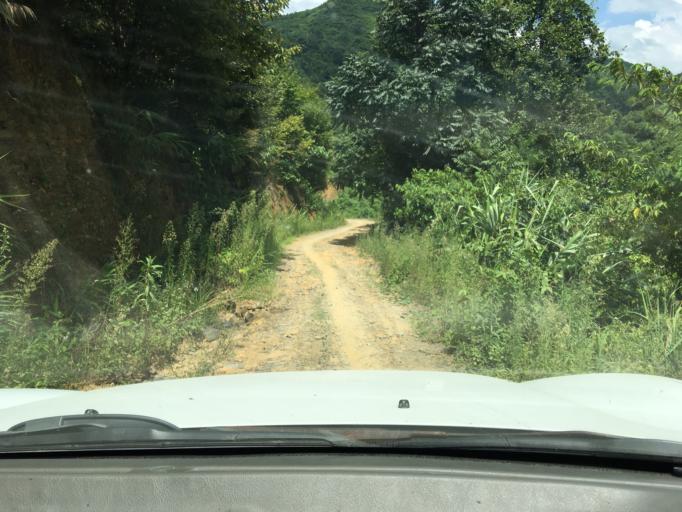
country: CN
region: Guangxi Zhuangzu Zizhiqu
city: Tongle
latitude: 24.9702
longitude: 105.9826
